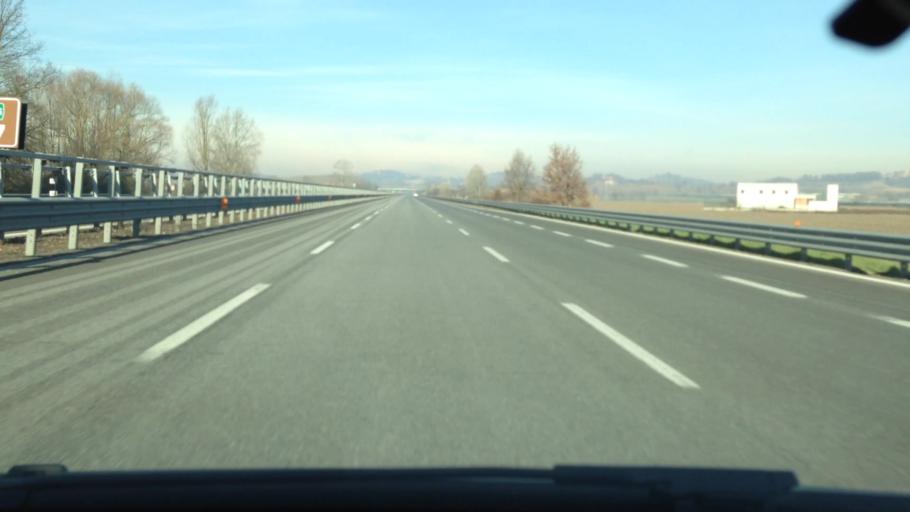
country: IT
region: Piedmont
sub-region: Provincia di Alessandria
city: Castelletto Monferrato
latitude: 44.9505
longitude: 8.5629
